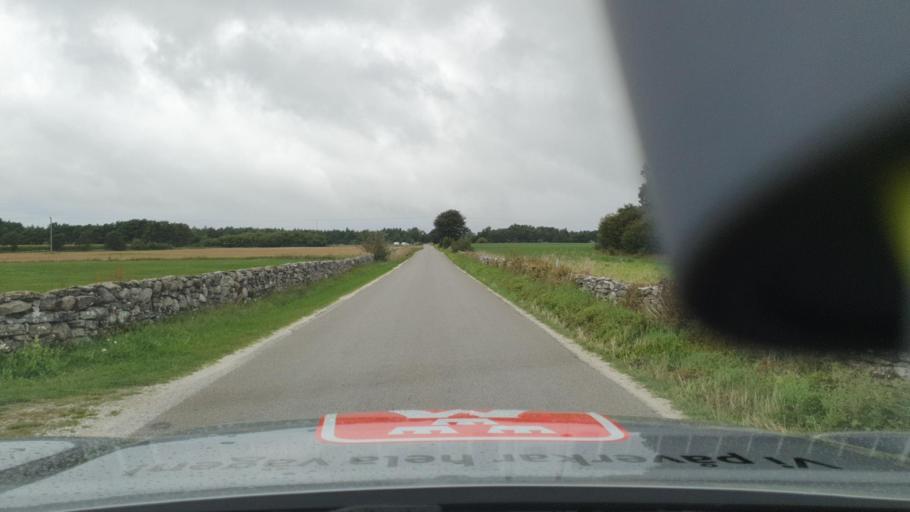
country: SE
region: Gotland
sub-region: Gotland
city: Hemse
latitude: 56.9424
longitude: 18.2604
